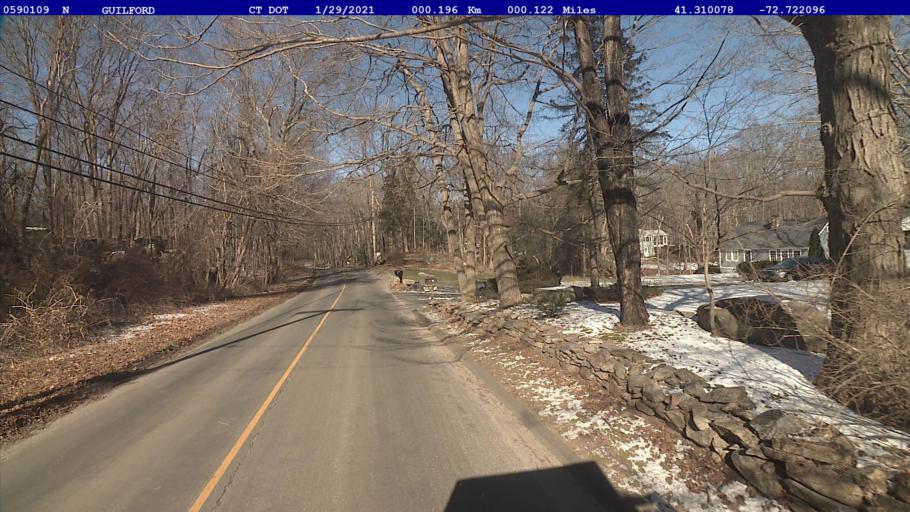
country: US
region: Connecticut
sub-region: New Haven County
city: Guilford
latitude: 41.3101
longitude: -72.7221
